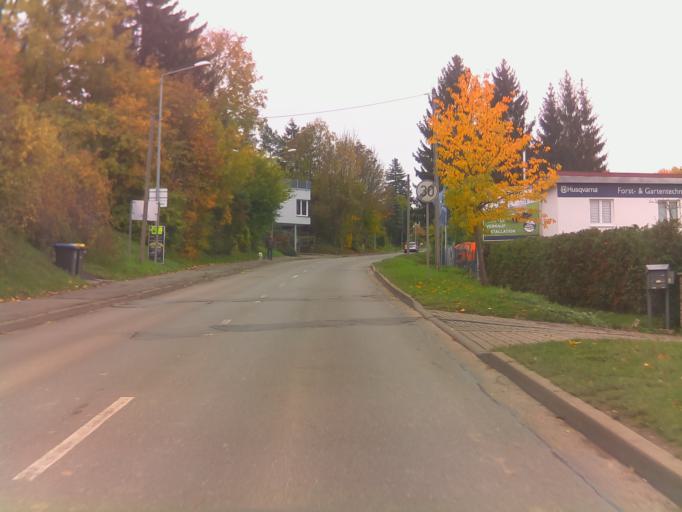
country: DE
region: Thuringia
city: Arnstadt
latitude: 50.8279
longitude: 10.9596
